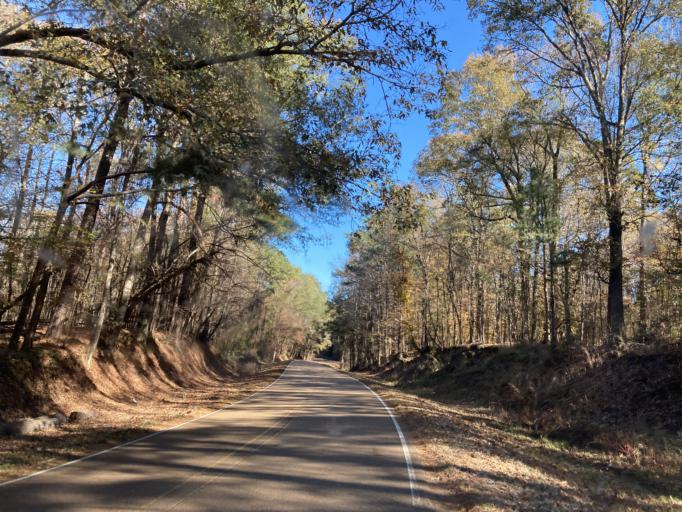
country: US
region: Mississippi
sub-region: Hinds County
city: Lynchburg
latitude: 32.5962
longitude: -90.5372
